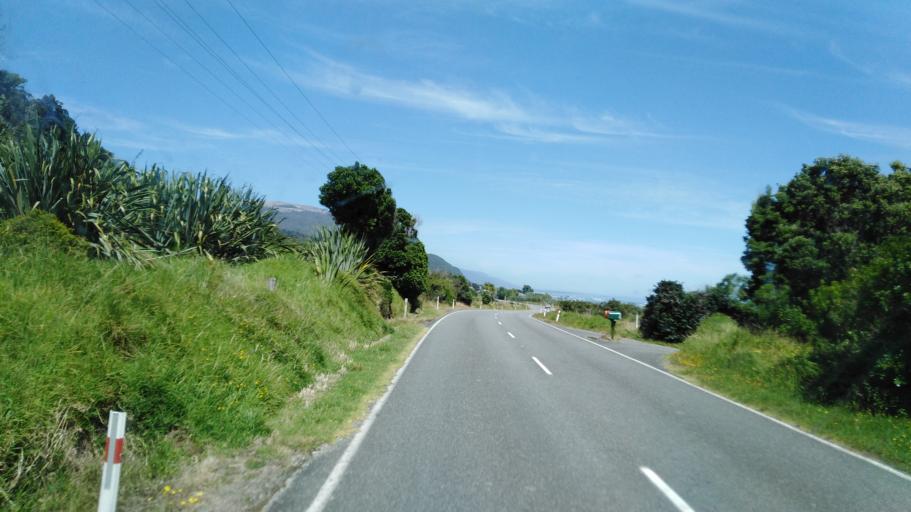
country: NZ
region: West Coast
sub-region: Buller District
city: Westport
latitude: -41.5951
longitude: 171.8878
